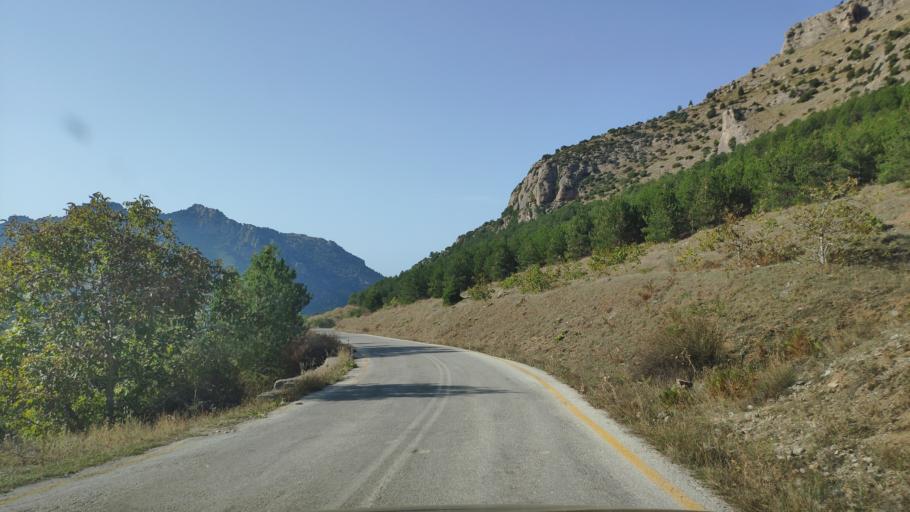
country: GR
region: West Greece
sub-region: Nomos Achaias
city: Aiyira
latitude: 38.0422
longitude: 22.3920
